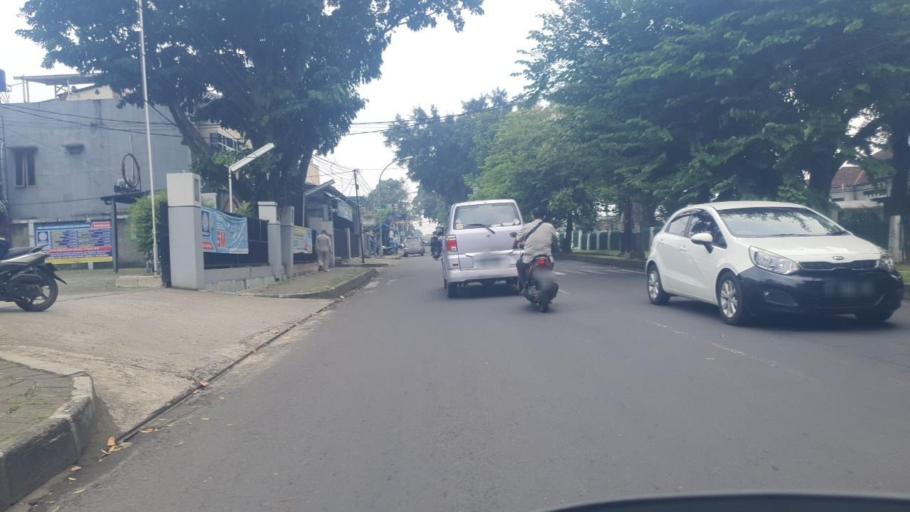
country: ID
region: West Java
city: Bogor
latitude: -6.5833
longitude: 106.7878
